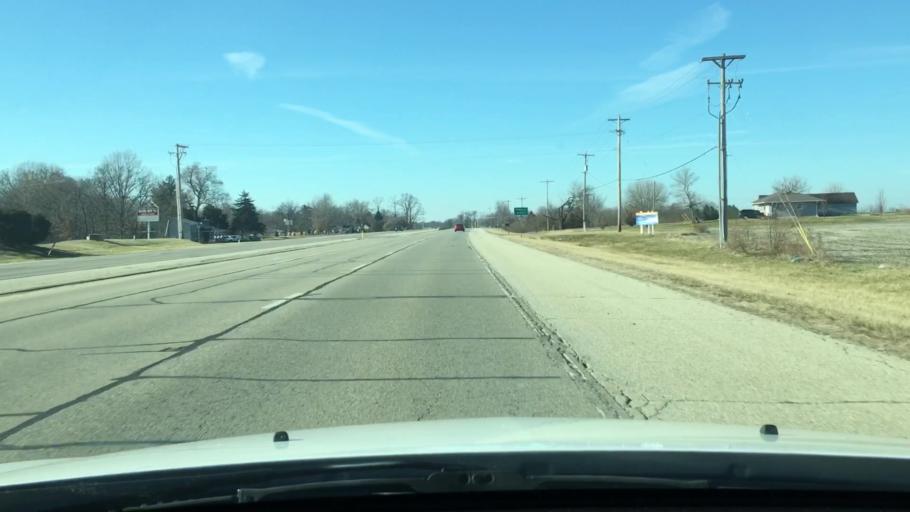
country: US
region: Illinois
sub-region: Woodford County
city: Germantown Hills
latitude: 40.7681
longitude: -89.4590
